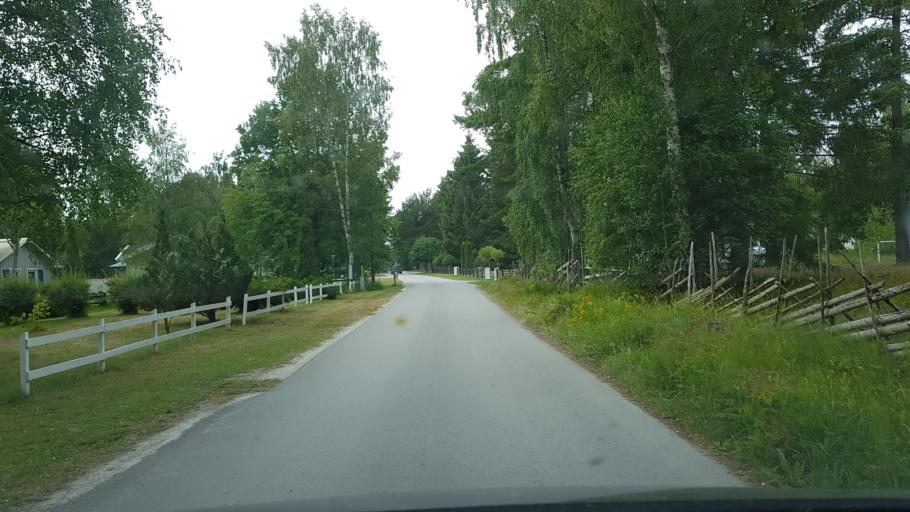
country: SE
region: Gotland
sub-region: Gotland
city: Hemse
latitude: 57.3382
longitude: 18.7146
